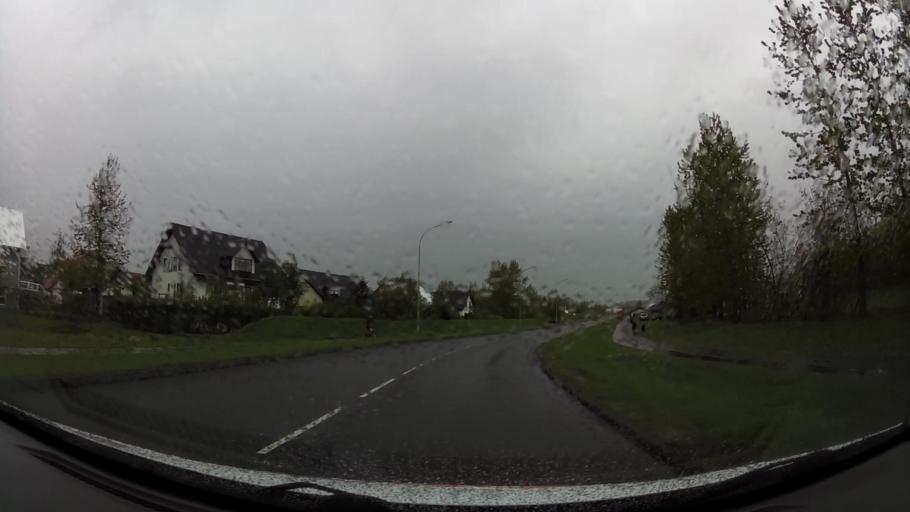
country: IS
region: Capital Region
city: Reykjavik
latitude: 64.0956
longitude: -21.8287
